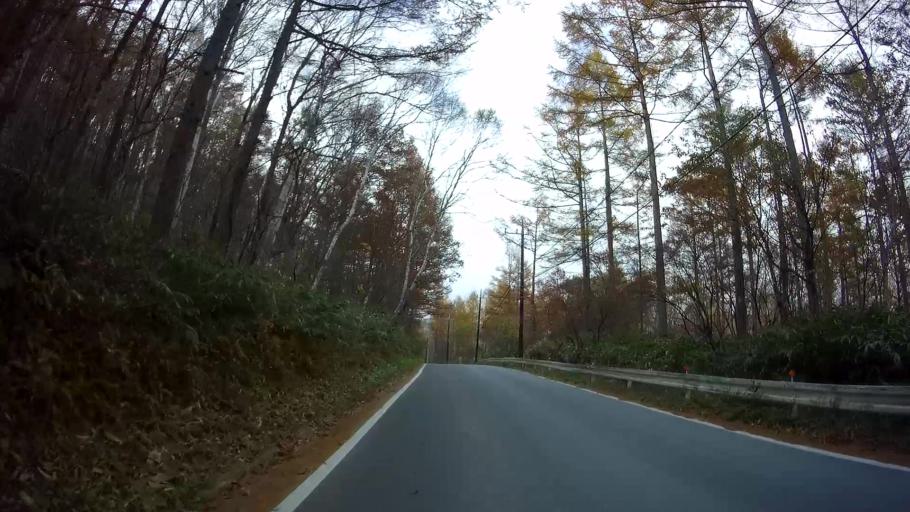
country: JP
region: Gunma
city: Nakanojomachi
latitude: 36.6709
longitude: 138.6714
